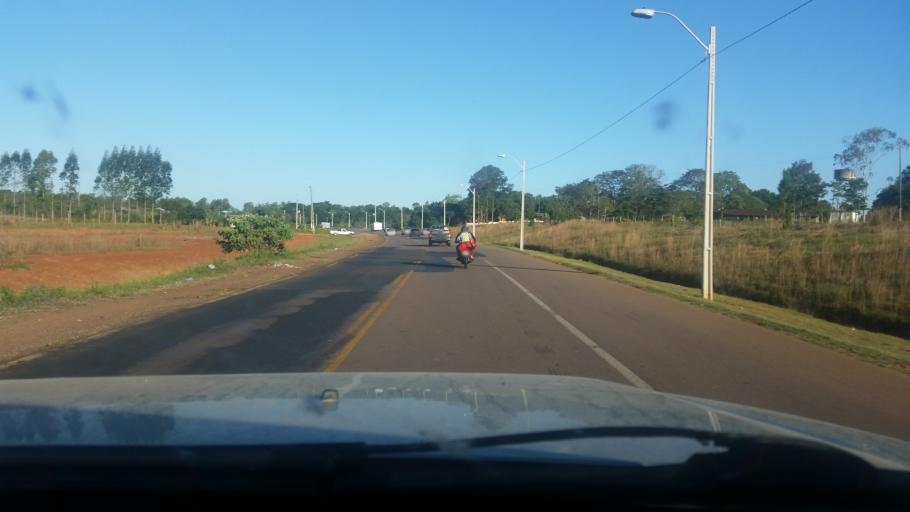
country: PY
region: Guaira
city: Villarrica
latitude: -25.7500
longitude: -56.4436
